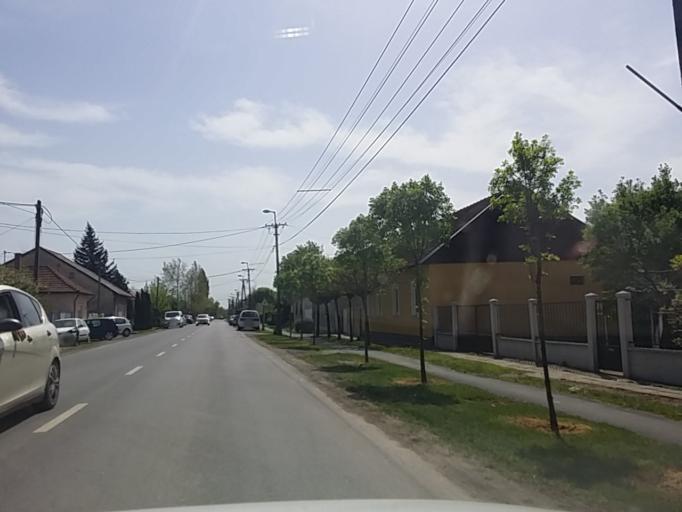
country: HU
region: Bekes
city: Gyula
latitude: 46.6605
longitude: 21.2783
